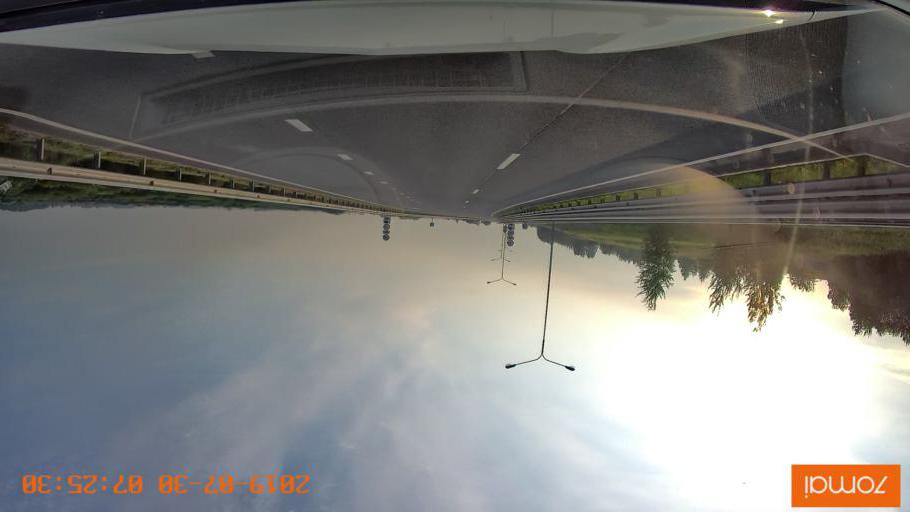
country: RU
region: Kaliningrad
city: Gvardeysk
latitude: 54.6864
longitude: 20.8364
